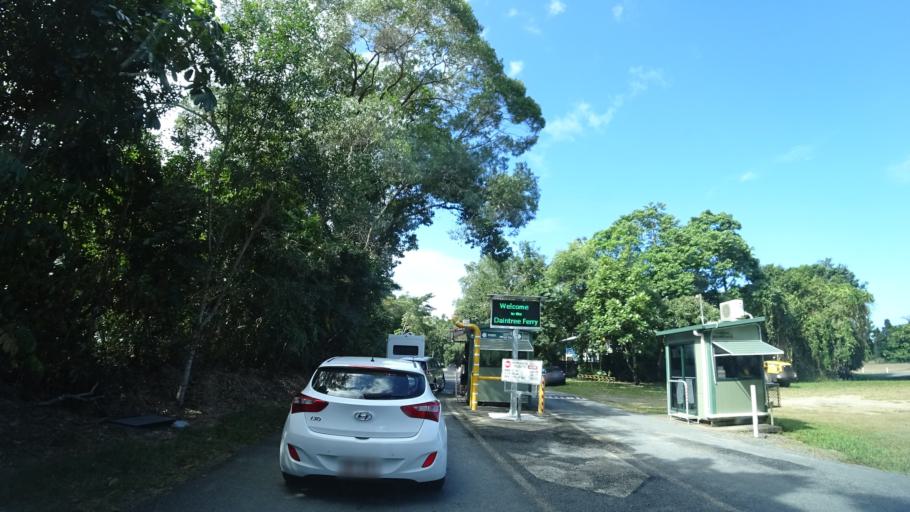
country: AU
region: Queensland
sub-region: Cairns
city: Port Douglas
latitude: -16.2613
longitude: 145.3963
